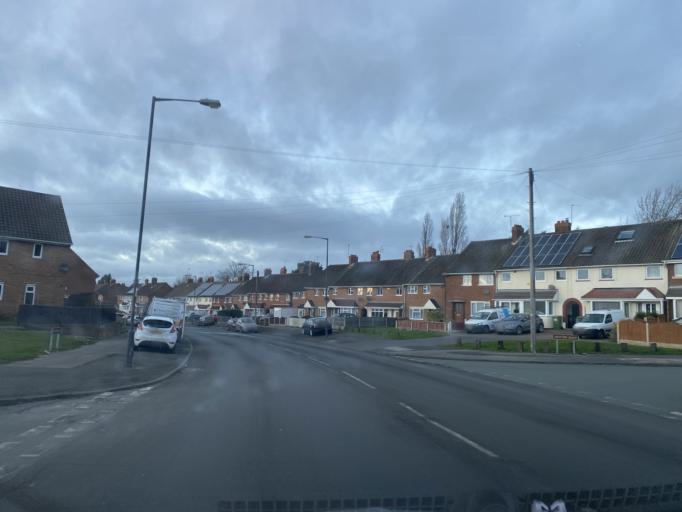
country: GB
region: England
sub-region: Walsall
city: Bloxwich
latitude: 52.6014
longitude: -2.0035
